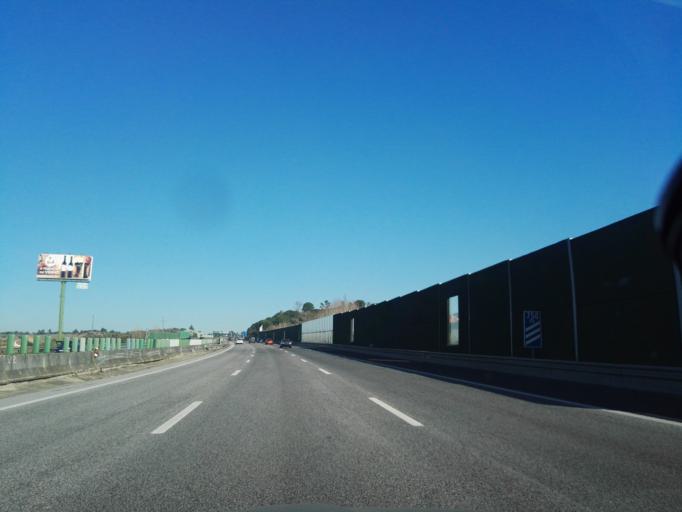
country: PT
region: Lisbon
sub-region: Azambuja
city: Aveiras de Cima
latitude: 39.1319
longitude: -8.8967
